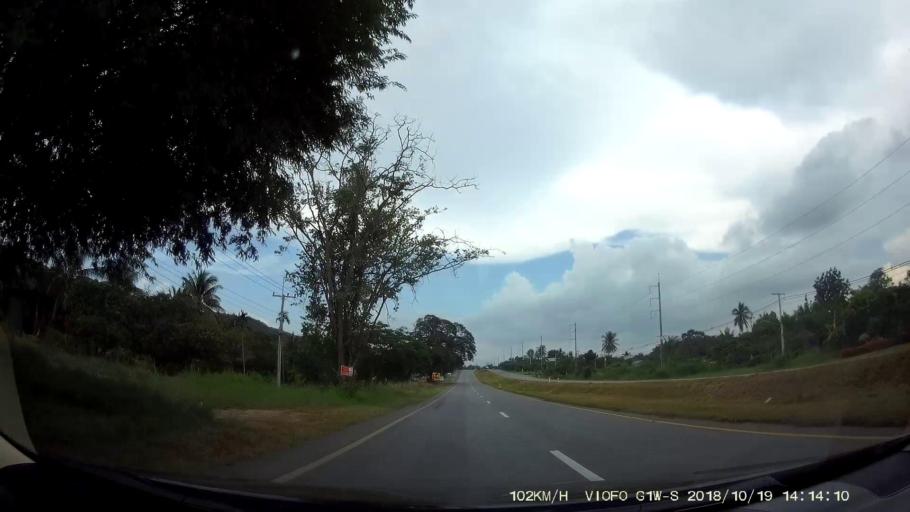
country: TH
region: Chaiyaphum
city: Khon Sawan
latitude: 15.9689
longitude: 102.1854
